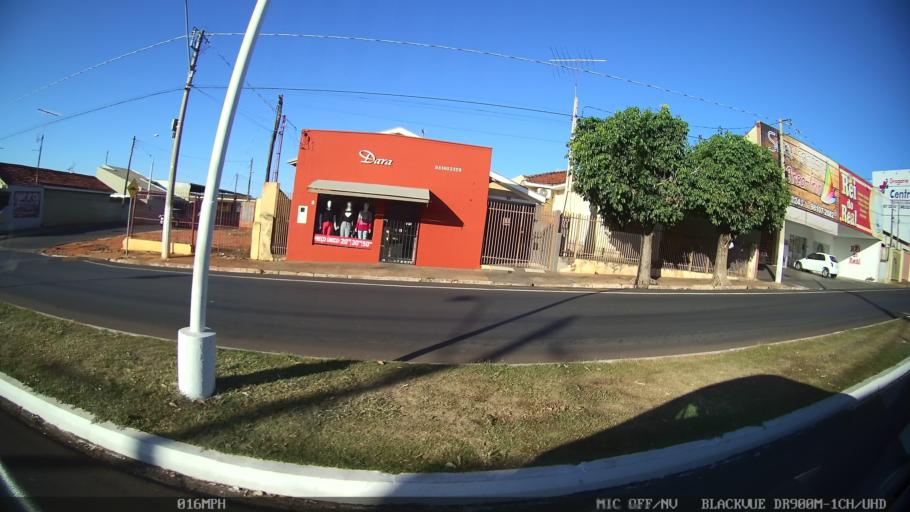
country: BR
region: Sao Paulo
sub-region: Guapiacu
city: Guapiacu
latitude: -20.7940
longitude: -49.2209
